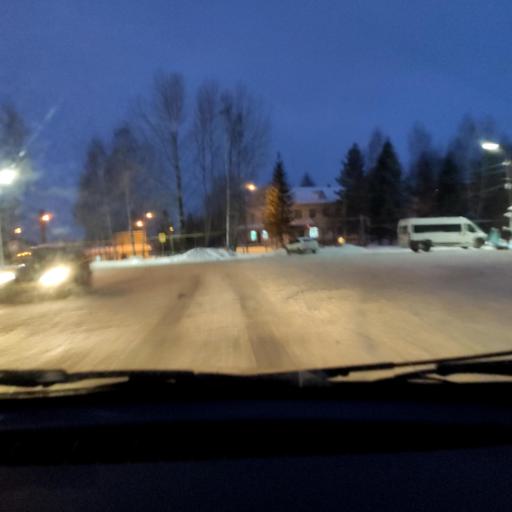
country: RU
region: Bashkortostan
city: Blagoveshchensk
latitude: 55.0488
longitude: 55.9484
